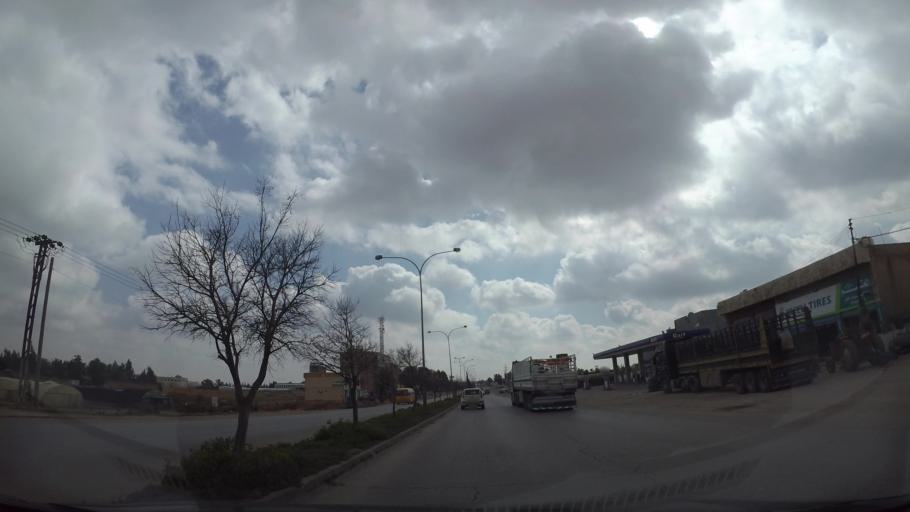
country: JO
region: Amman
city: Jawa
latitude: 31.8246
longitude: 35.9111
